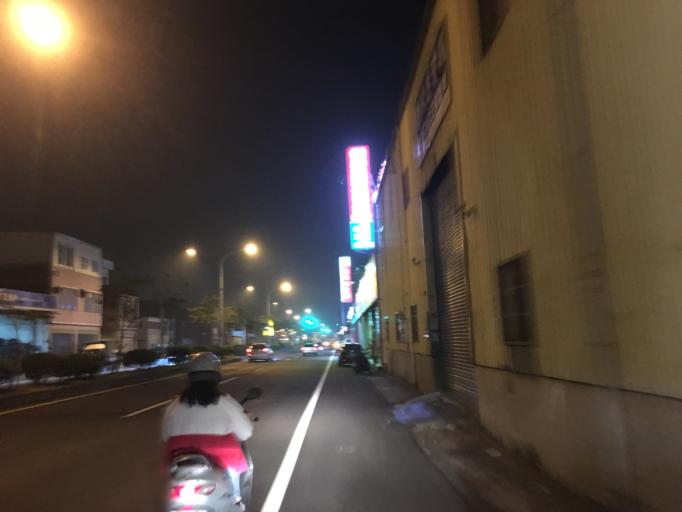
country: TW
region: Taiwan
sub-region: Miaoli
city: Miaoli
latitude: 24.6735
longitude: 120.8831
